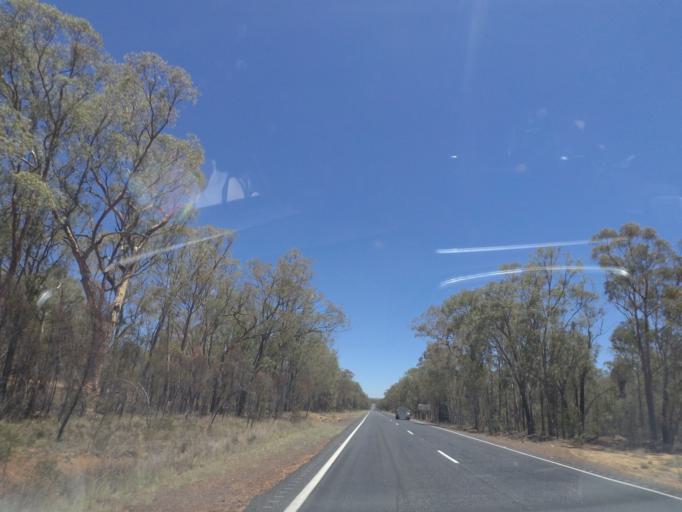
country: AU
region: New South Wales
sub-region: Warrumbungle Shire
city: Coonabarabran
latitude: -31.2149
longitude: 149.3281
